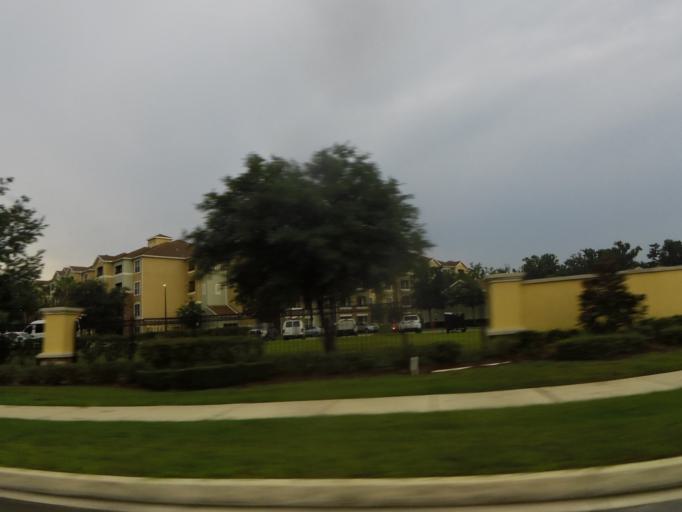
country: US
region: Florida
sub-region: Duval County
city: Jacksonville
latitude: 30.2547
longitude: -81.5640
